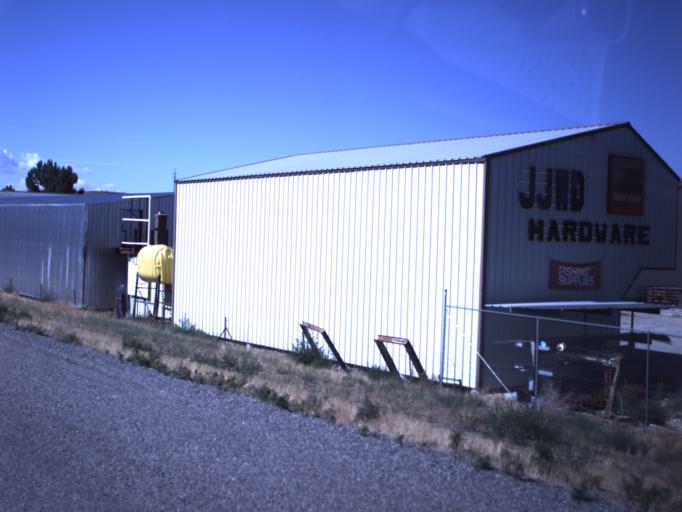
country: US
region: Utah
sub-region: Sevier County
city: Salina
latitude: 38.9526
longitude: -111.8601
